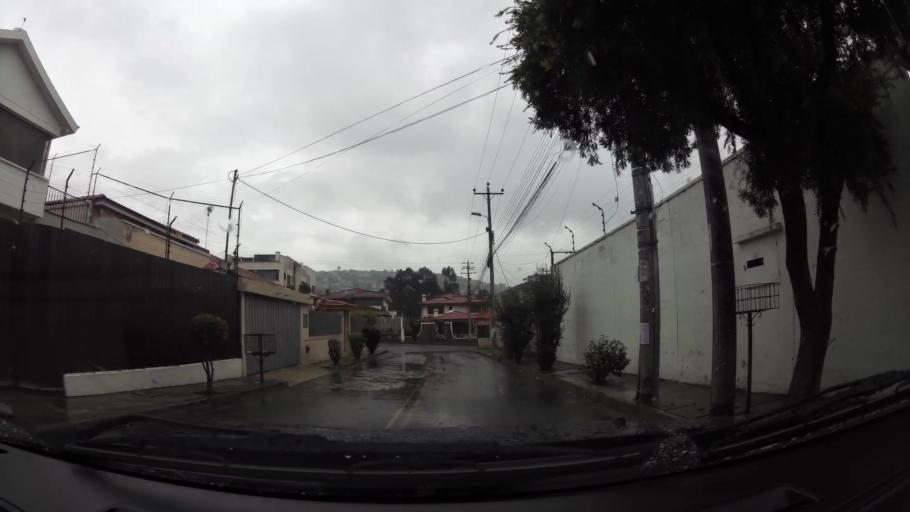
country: EC
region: Pichincha
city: Quito
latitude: -0.1019
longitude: -78.5020
